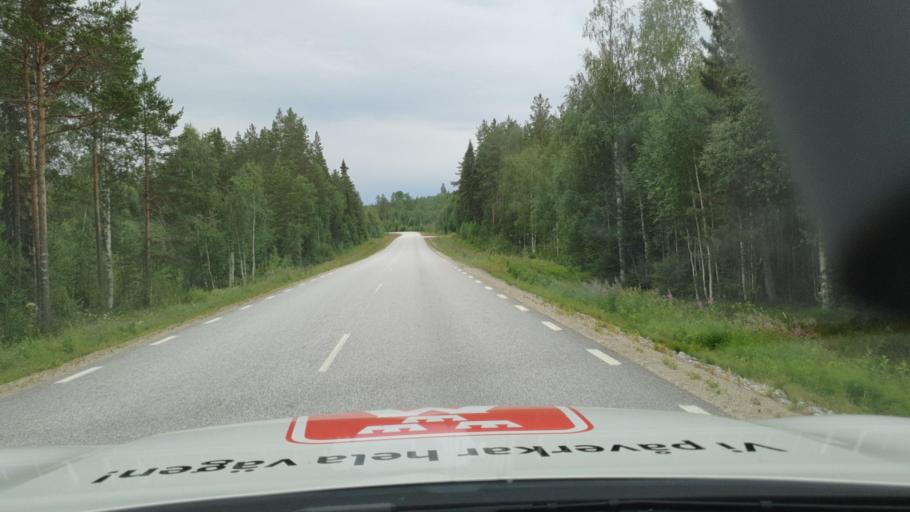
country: SE
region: Vaesterbotten
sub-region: Vindelns Kommun
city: Vindeln
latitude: 64.1886
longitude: 19.4057
